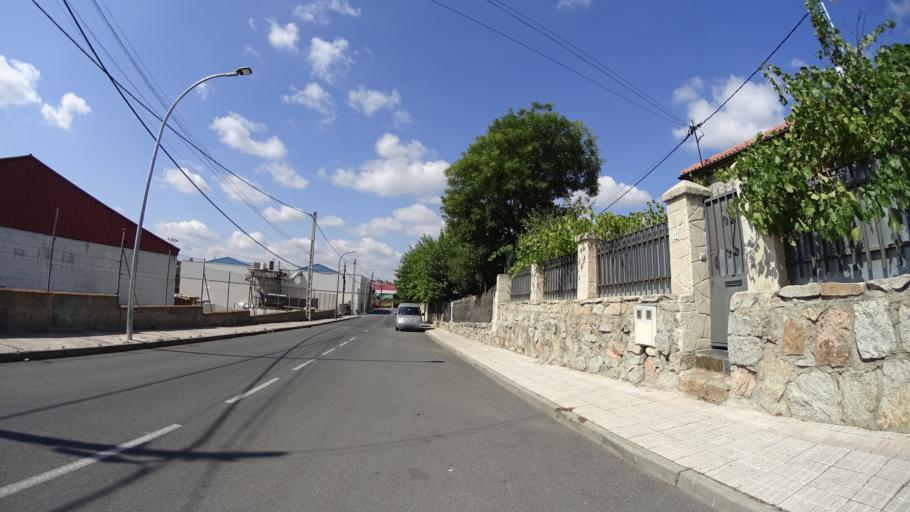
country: ES
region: Madrid
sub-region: Provincia de Madrid
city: Galapagar
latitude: 40.5826
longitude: -3.9951
